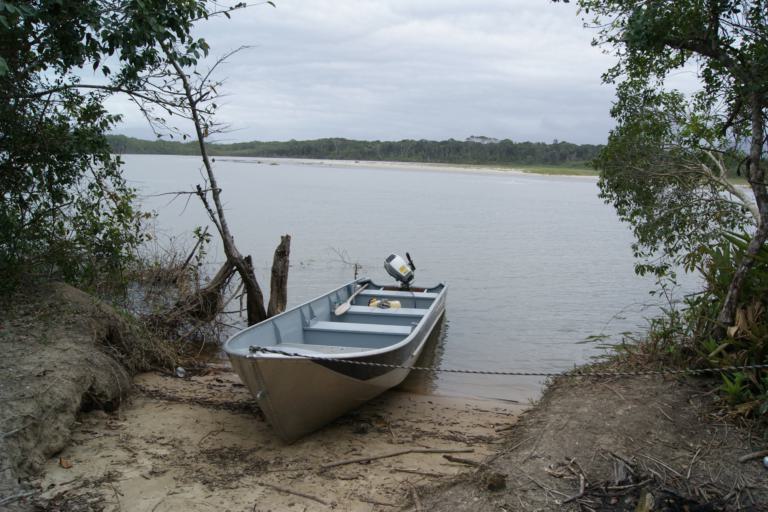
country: BR
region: Sao Paulo
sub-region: Peruibe
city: Peruibe
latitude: -24.4410
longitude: -47.0780
